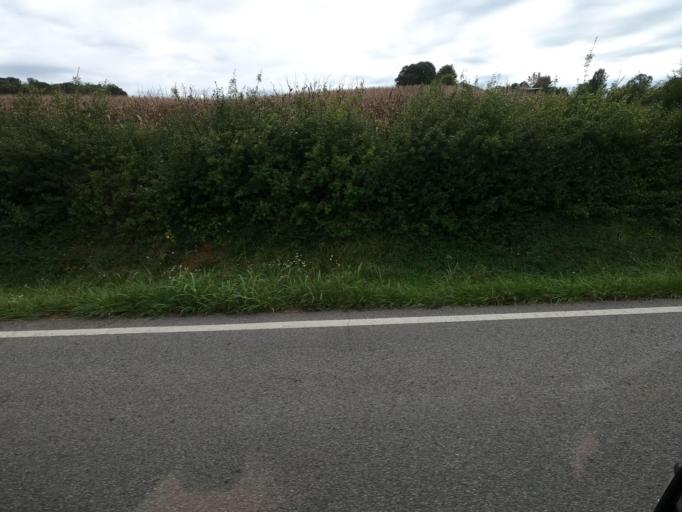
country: US
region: Tennessee
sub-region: Washington County
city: Jonesborough
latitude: 36.2439
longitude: -82.5561
